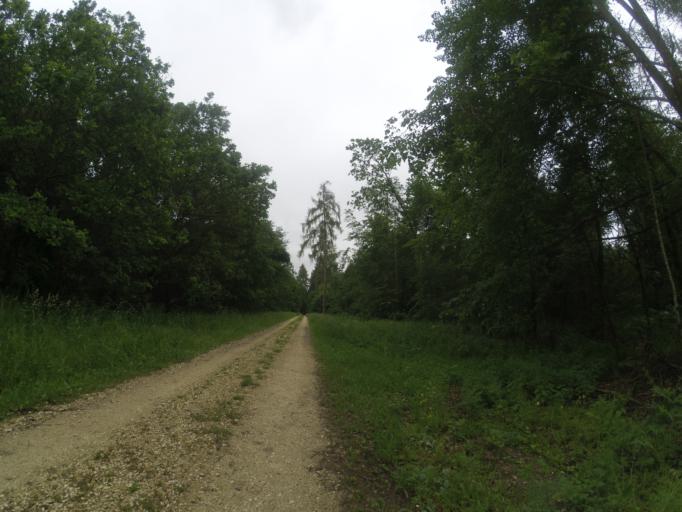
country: DE
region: Baden-Wuerttemberg
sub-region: Tuebingen Region
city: Borslingen
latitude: 48.5154
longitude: 10.0591
